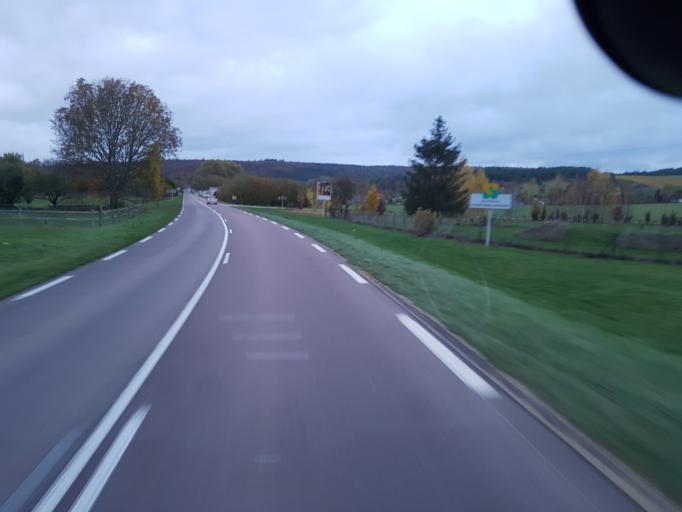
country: FR
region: Champagne-Ardenne
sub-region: Departement de l'Aube
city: Mussy-sur-Seine
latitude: 47.9703
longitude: 4.5010
